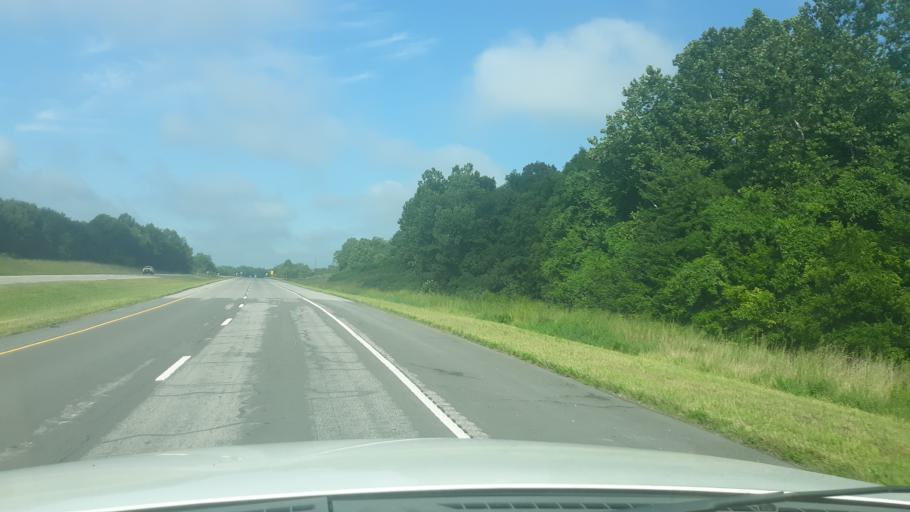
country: US
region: Illinois
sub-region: Saline County
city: Carrier Mills
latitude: 37.7381
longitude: -88.7148
